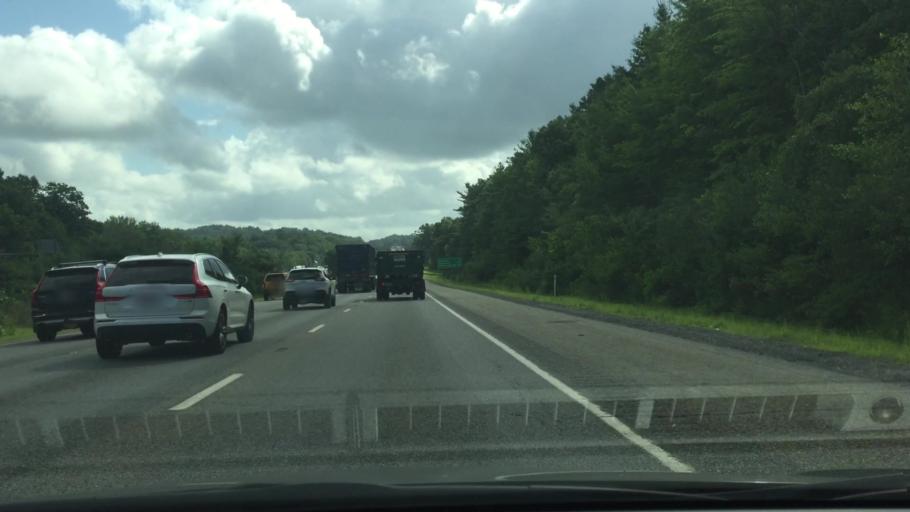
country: US
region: Massachusetts
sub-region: Middlesex County
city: Littleton Common
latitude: 42.5526
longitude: -71.4632
